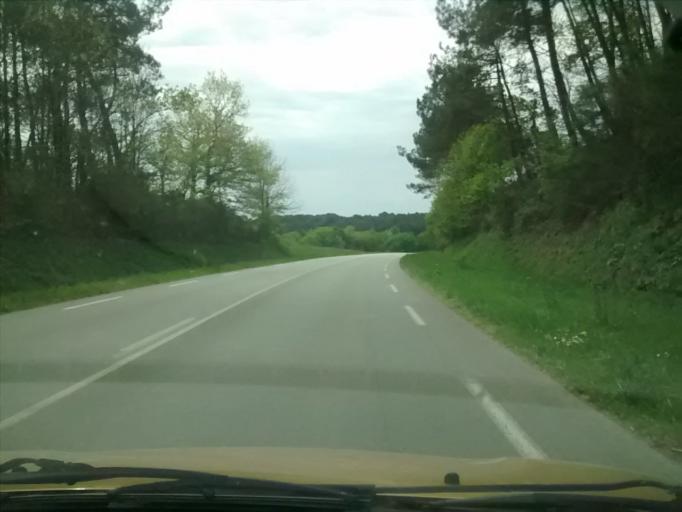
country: FR
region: Brittany
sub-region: Departement du Morbihan
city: Berric
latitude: 47.6094
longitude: -2.5407
